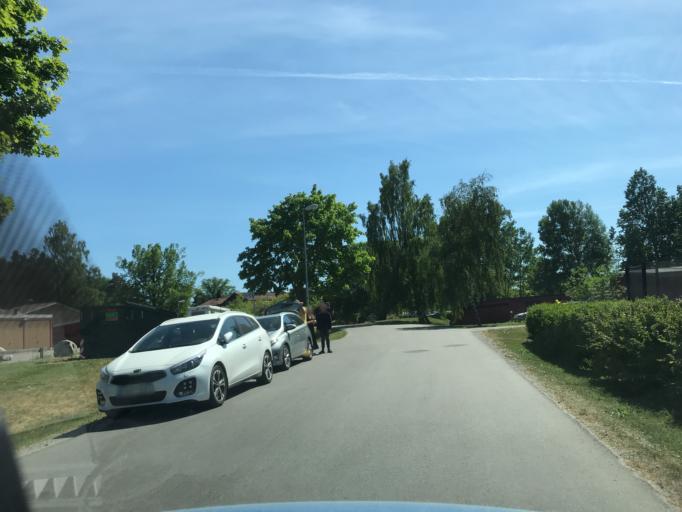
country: SE
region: Stockholm
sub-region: Stockholms Kommun
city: Kista
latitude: 59.4063
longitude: 17.9782
